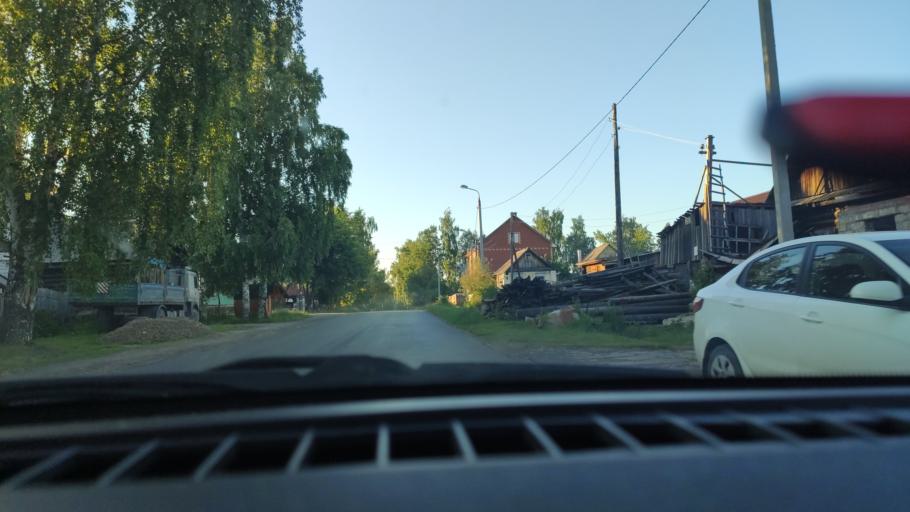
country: RU
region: Perm
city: Polazna
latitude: 58.1184
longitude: 56.3943
